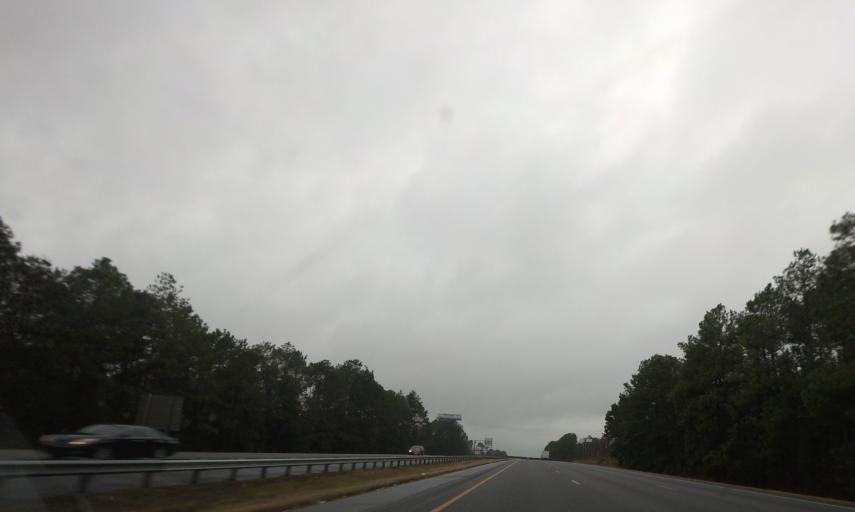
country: US
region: Georgia
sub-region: Lowndes County
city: Valdosta
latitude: 30.6902
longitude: -83.2344
